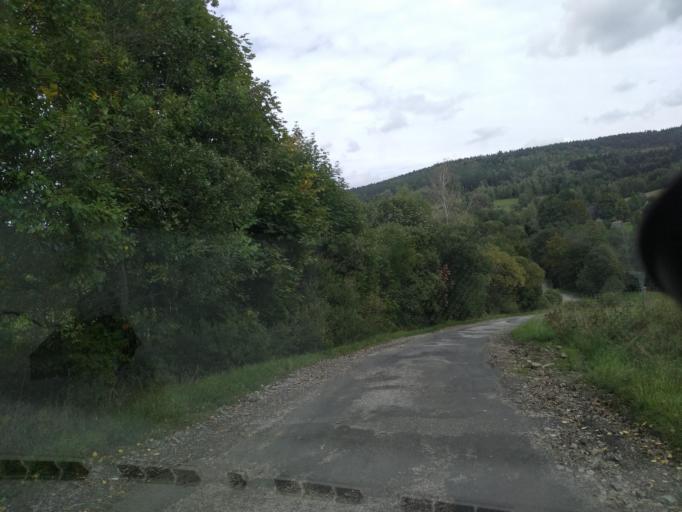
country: PL
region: Lesser Poland Voivodeship
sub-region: Powiat gorlicki
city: Uscie Gorlickie
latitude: 49.5465
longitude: 21.1857
